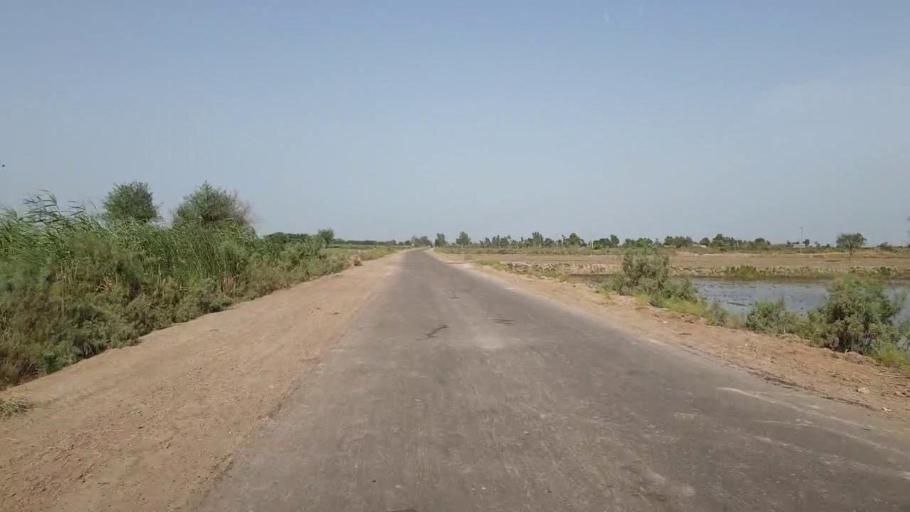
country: PK
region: Sindh
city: Sakrand
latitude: 26.2845
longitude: 68.2448
